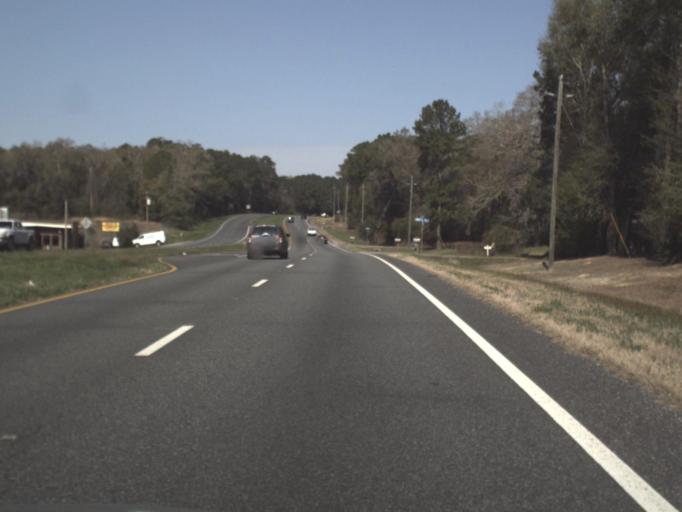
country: US
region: Florida
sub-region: Gadsden County
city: Midway
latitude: 30.5352
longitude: -84.3650
